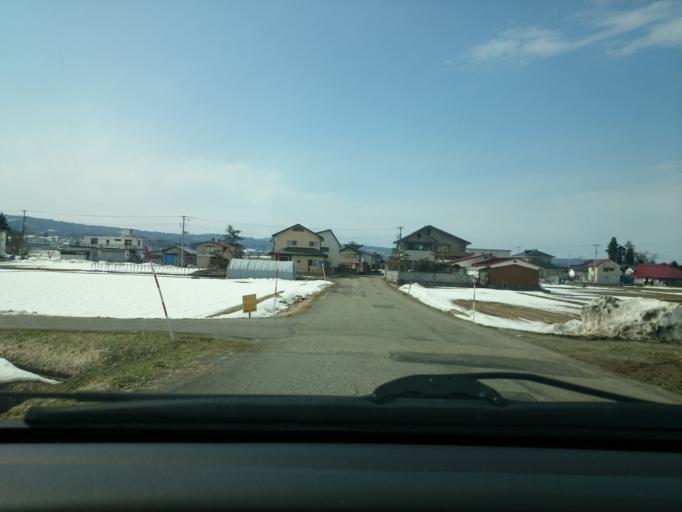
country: JP
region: Fukushima
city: Kitakata
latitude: 37.5156
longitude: 139.8444
